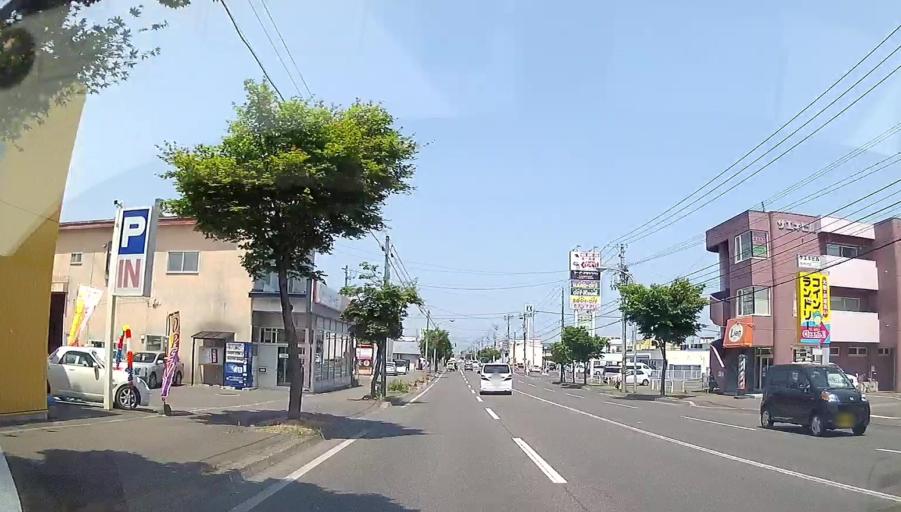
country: JP
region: Hokkaido
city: Obihiro
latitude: 42.8956
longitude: 143.2008
